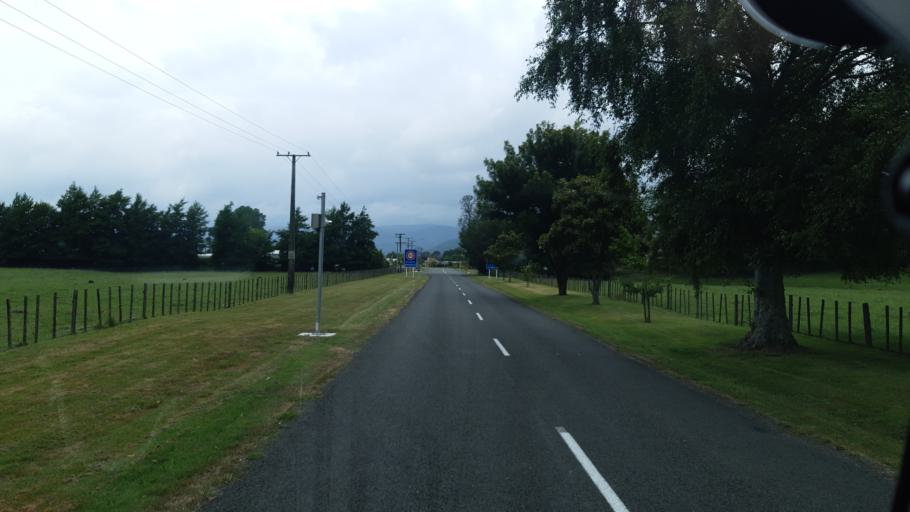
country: NZ
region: Waikato
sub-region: South Waikato District
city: Tokoroa
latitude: -38.3753
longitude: 175.7671
